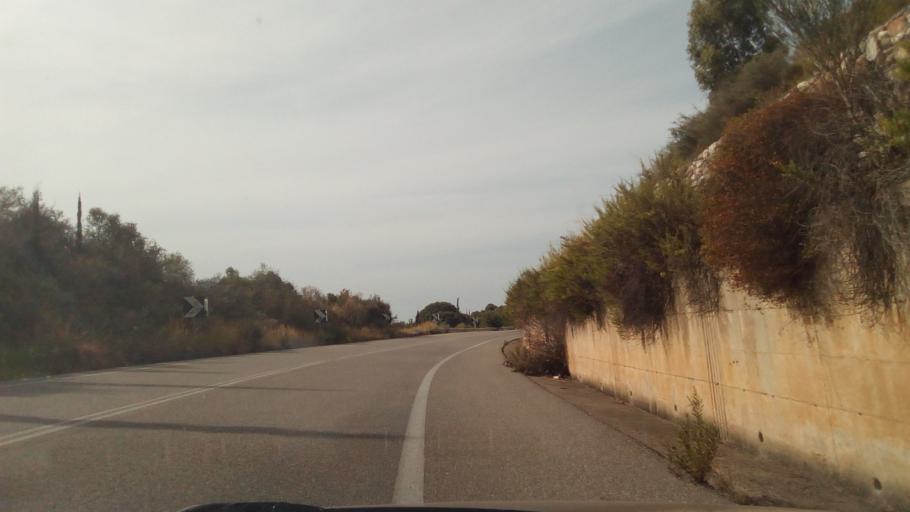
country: GR
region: West Greece
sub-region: Nomos Aitolias kai Akarnanias
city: Nafpaktos
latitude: 38.3861
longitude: 21.7961
